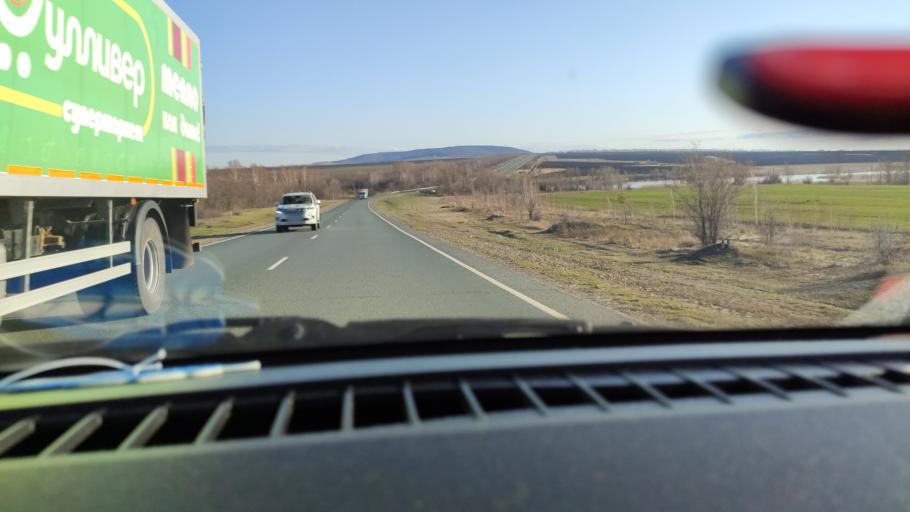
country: RU
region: Saratov
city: Alekseyevka
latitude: 52.2429
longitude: 47.9068
